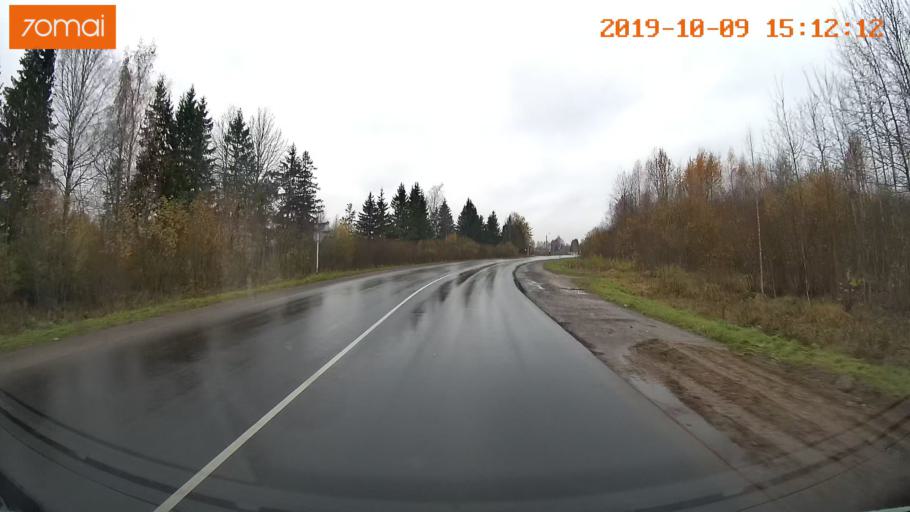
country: RU
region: Kostroma
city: Susanino
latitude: 58.1564
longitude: 41.6214
